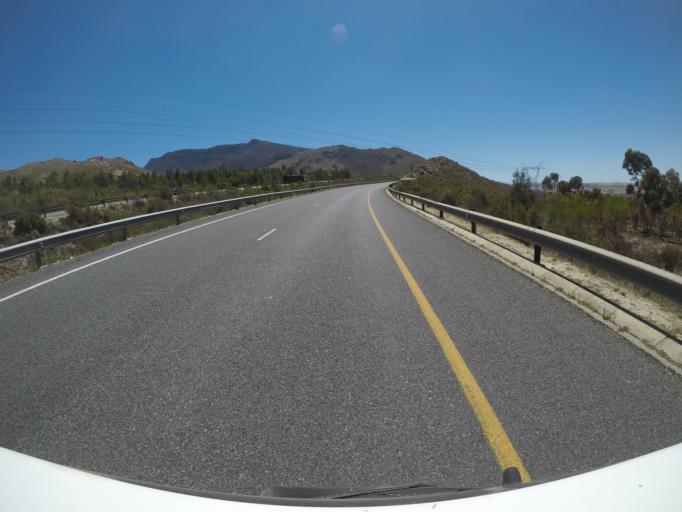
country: ZA
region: Western Cape
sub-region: Overberg District Municipality
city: Grabouw
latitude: -34.2219
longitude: 19.1881
